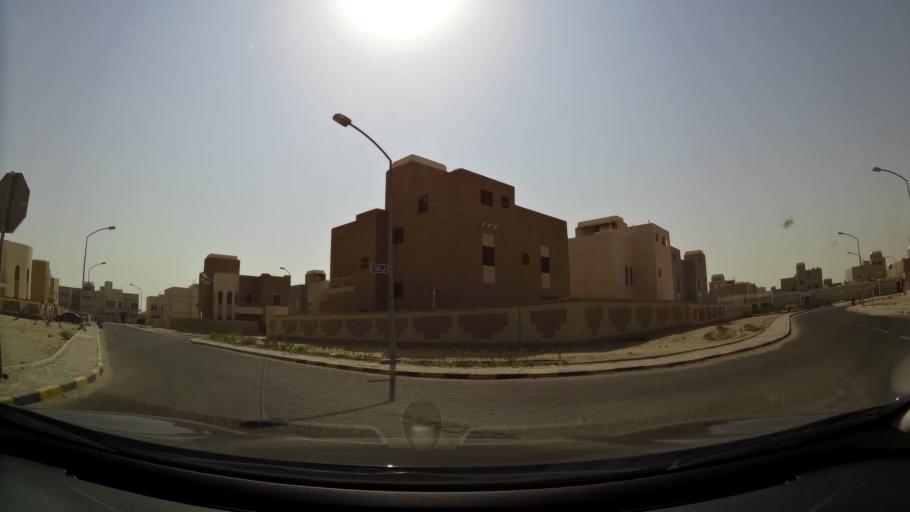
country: KW
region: Al Ahmadi
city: Al Wafrah
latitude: 28.8023
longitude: 48.0573
